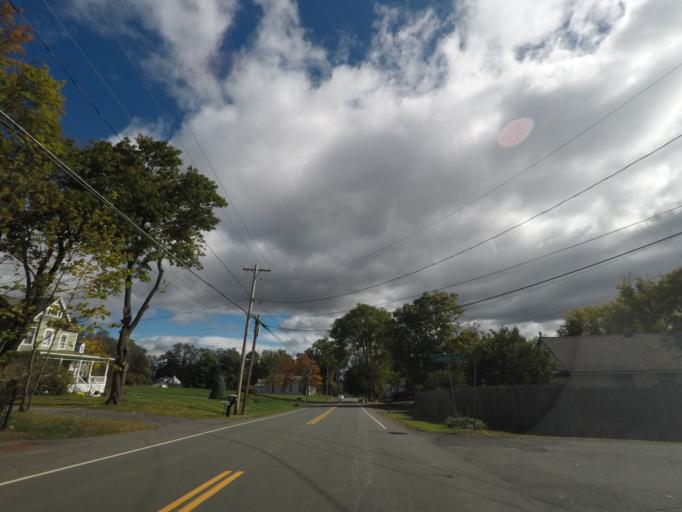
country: US
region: New York
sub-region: Albany County
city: Cohoes
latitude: 42.7834
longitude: -73.7422
